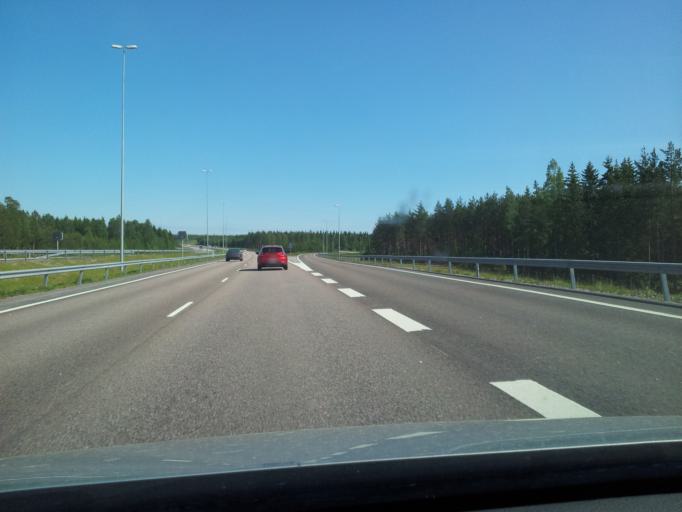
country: FI
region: Uusimaa
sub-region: Loviisa
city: Lovisa
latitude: 60.4658
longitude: 26.1356
